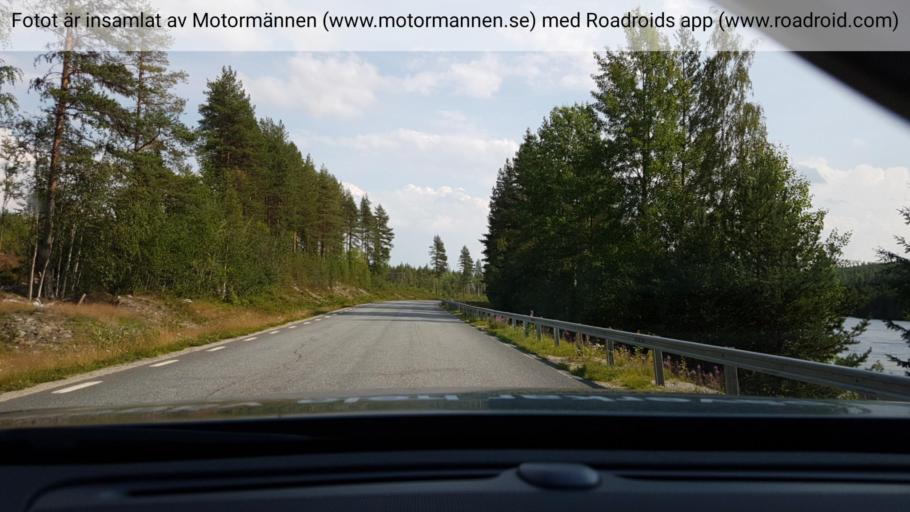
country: SE
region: Vaesterbotten
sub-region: Lycksele Kommun
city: Lycksele
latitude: 64.4040
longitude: 19.0318
